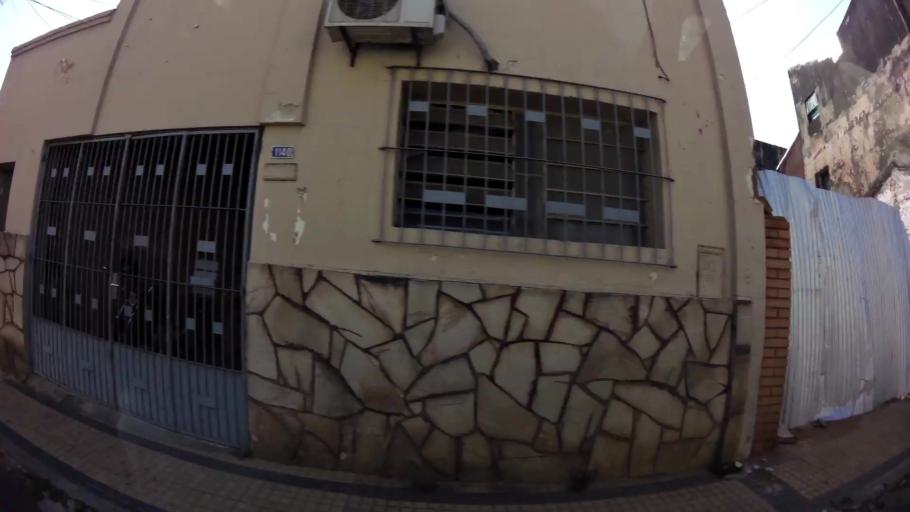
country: PY
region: Asuncion
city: Asuncion
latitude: -25.3010
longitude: -57.6198
